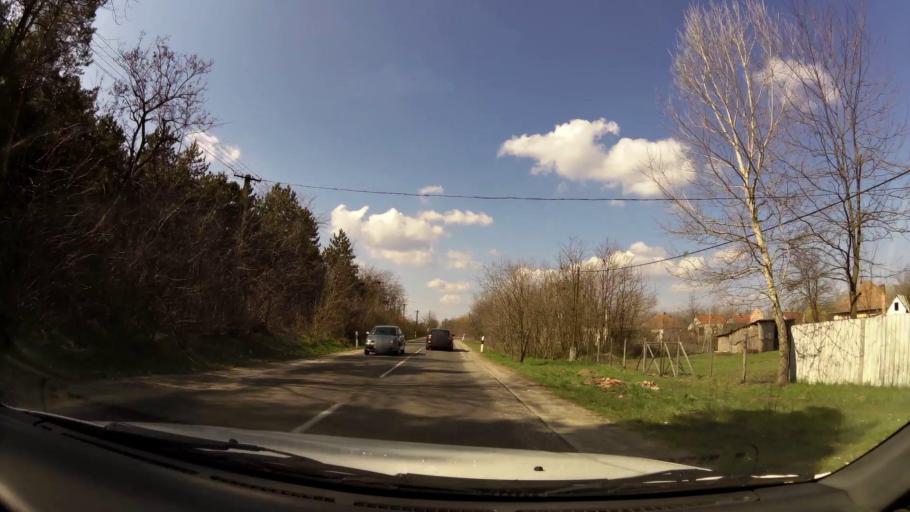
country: HU
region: Pest
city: Farmos
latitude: 47.3702
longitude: 19.7974
